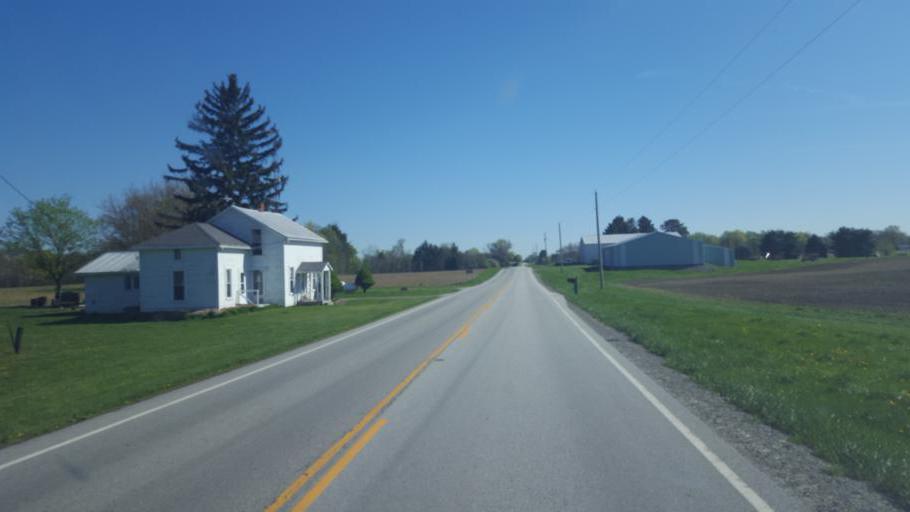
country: US
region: Ohio
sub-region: Wyandot County
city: Upper Sandusky
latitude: 40.8975
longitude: -83.2303
